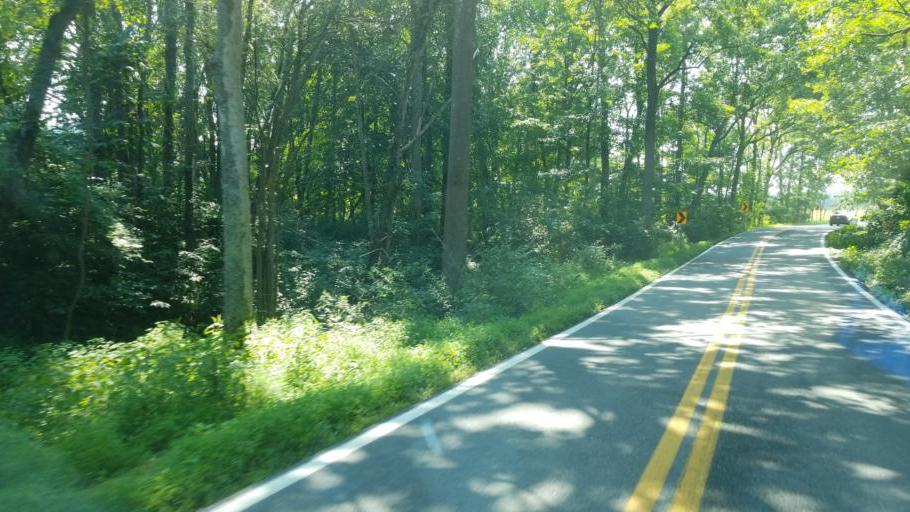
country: US
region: Virginia
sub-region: Frederick County
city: Shawnee Land
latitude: 39.4043
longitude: -78.4268
